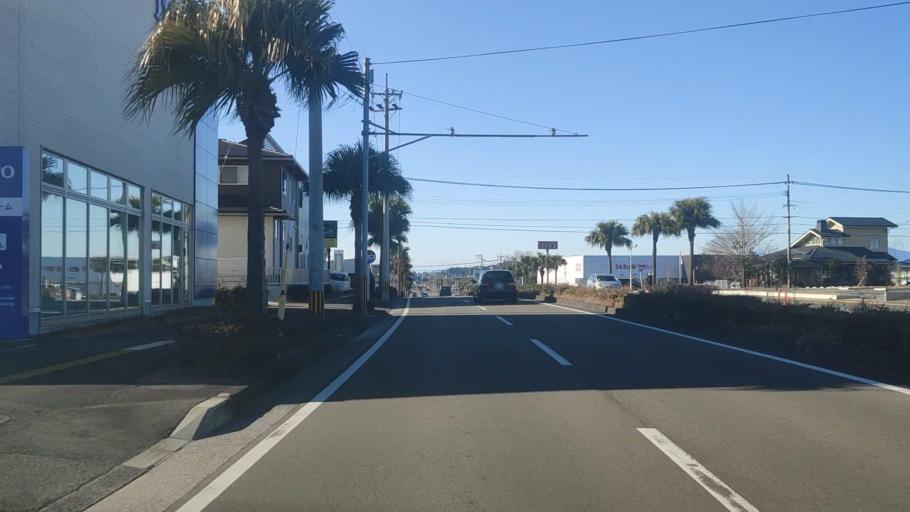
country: JP
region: Miyazaki
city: Miyazaki-shi
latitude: 31.9417
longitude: 131.4470
